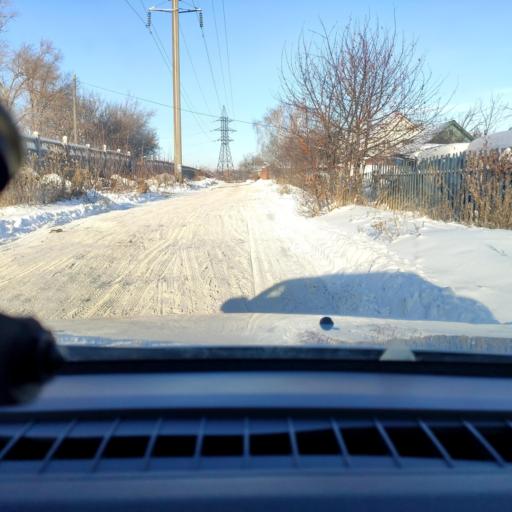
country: RU
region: Samara
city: Petra-Dubrava
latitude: 53.3101
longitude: 50.2979
